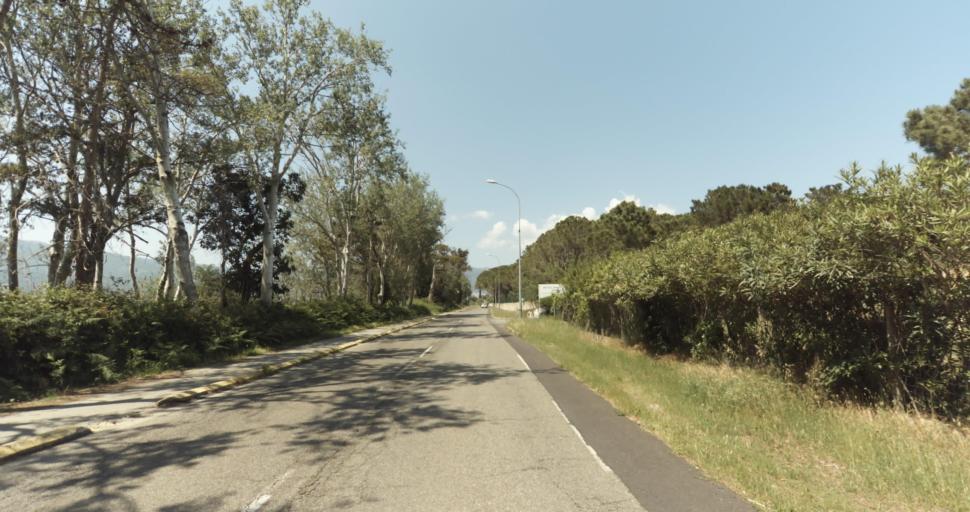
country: FR
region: Corsica
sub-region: Departement de la Haute-Corse
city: Biguglia
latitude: 42.6330
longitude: 9.4638
